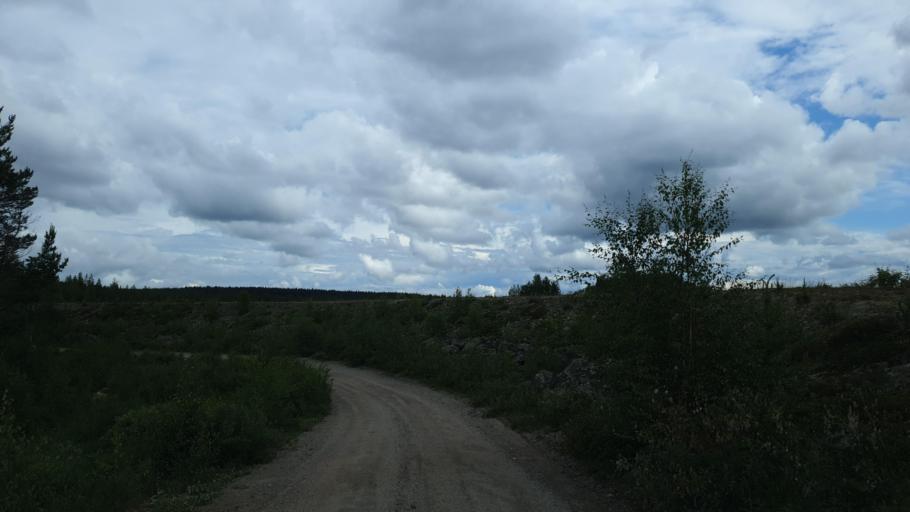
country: SE
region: Jaemtland
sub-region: Harjedalens Kommun
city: Sveg
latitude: 62.0418
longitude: 14.4845
